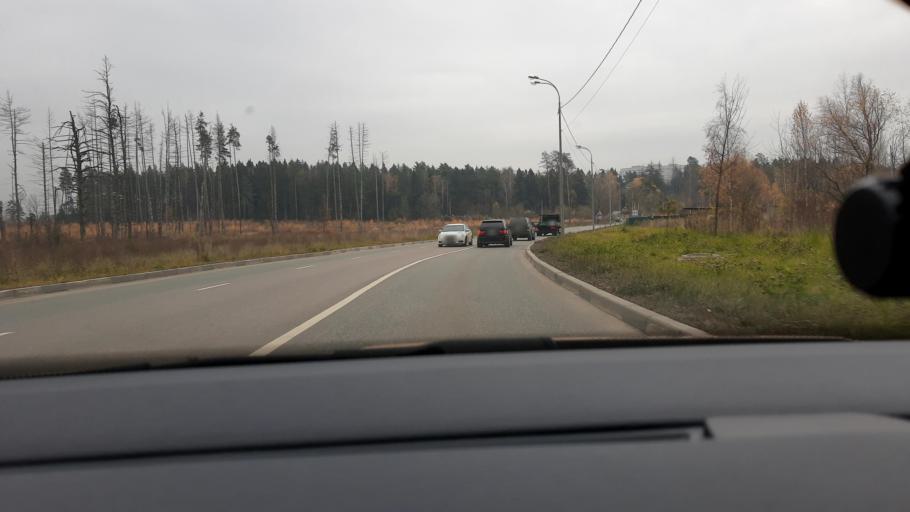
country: RU
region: Moskovskaya
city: Pirogovskiy
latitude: 55.9447
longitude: 37.7572
